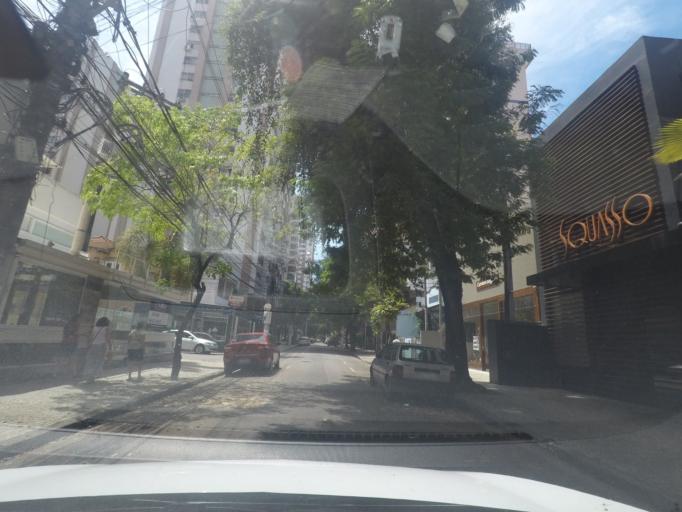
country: BR
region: Rio de Janeiro
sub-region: Niteroi
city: Niteroi
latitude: -22.9060
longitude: -43.1096
